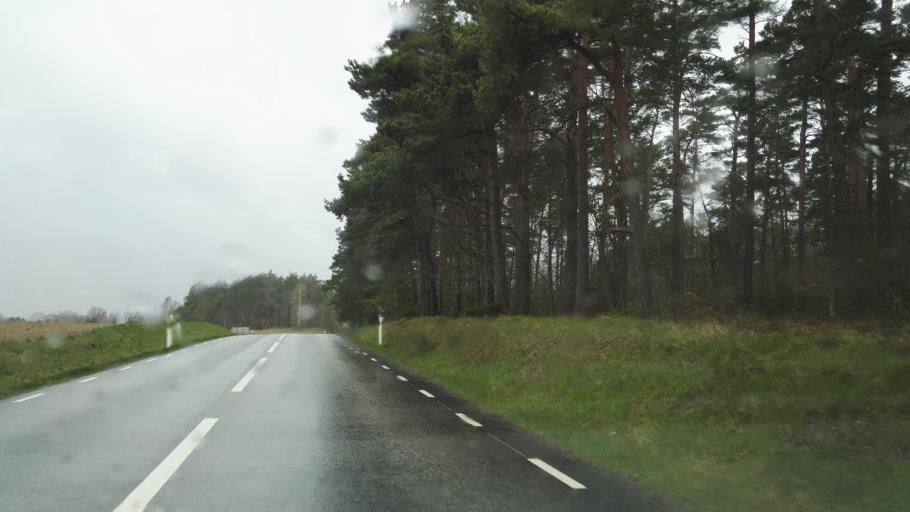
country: SE
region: Skane
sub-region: Simrishamns Kommun
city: Kivik
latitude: 55.7124
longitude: 14.1615
